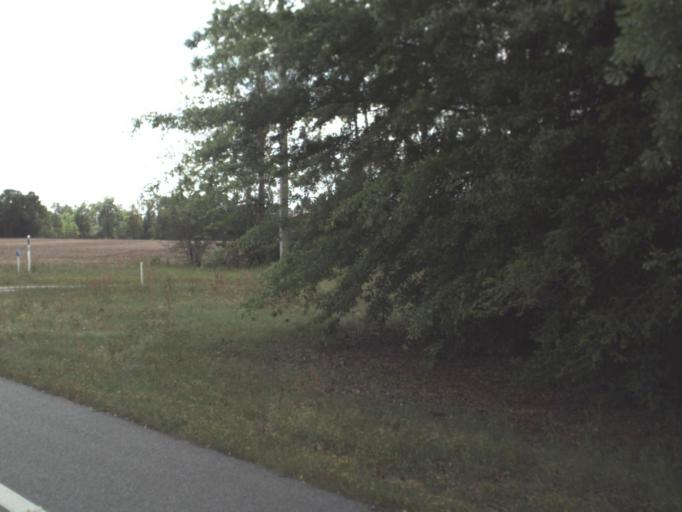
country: US
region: Alabama
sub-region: Escambia County
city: Atmore
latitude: 30.9201
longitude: -87.4800
